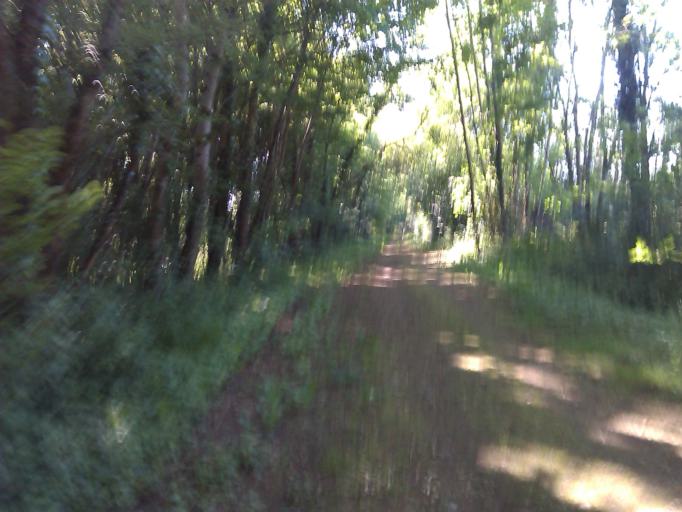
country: FR
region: Centre
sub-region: Departement de l'Indre
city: Belabre
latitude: 46.6304
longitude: 1.1815
